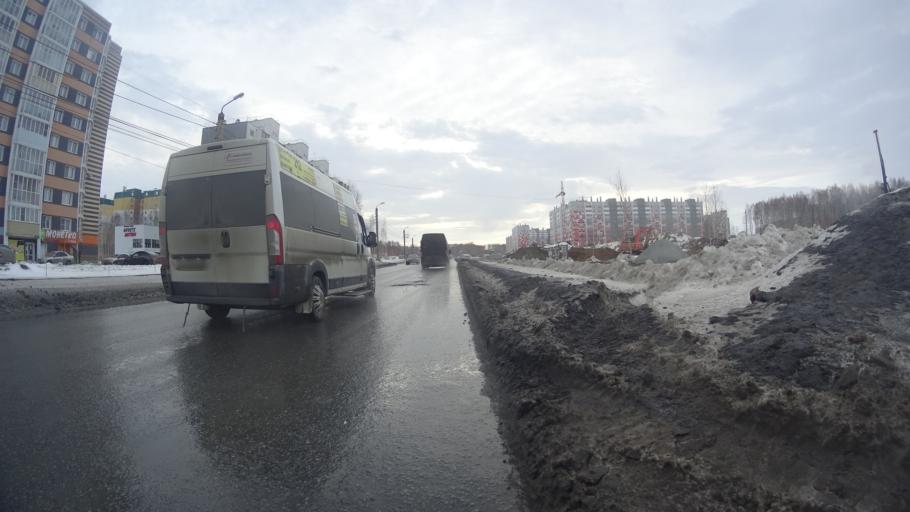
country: RU
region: Chelyabinsk
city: Roshchino
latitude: 55.2191
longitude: 61.2939
